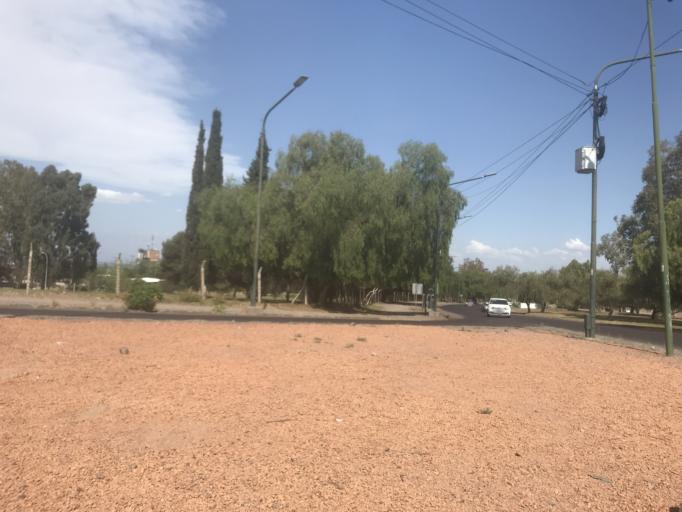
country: AR
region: Mendoza
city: Mendoza
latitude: -32.8819
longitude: -68.8825
